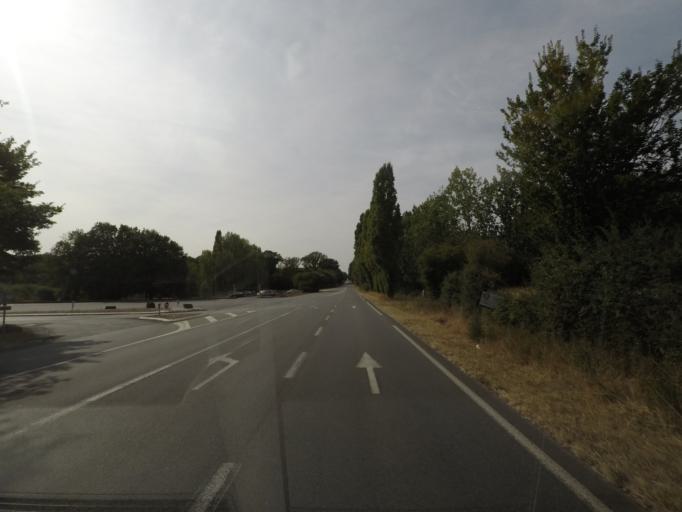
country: FR
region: Poitou-Charentes
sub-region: Departement des Deux-Sevres
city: Chef-Boutonne
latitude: 46.1816
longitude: -0.0278
